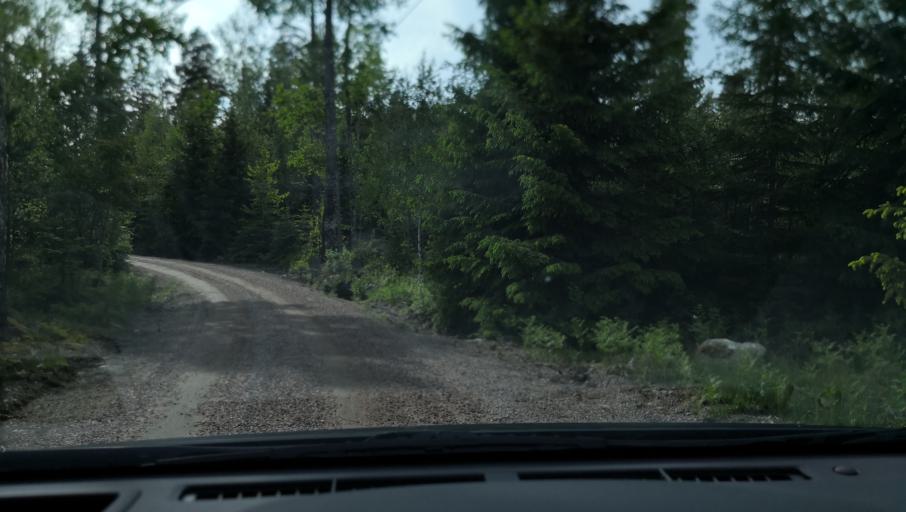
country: SE
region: Vaestmanland
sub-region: Arboga Kommun
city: Tyringe
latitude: 59.3438
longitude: 15.9165
